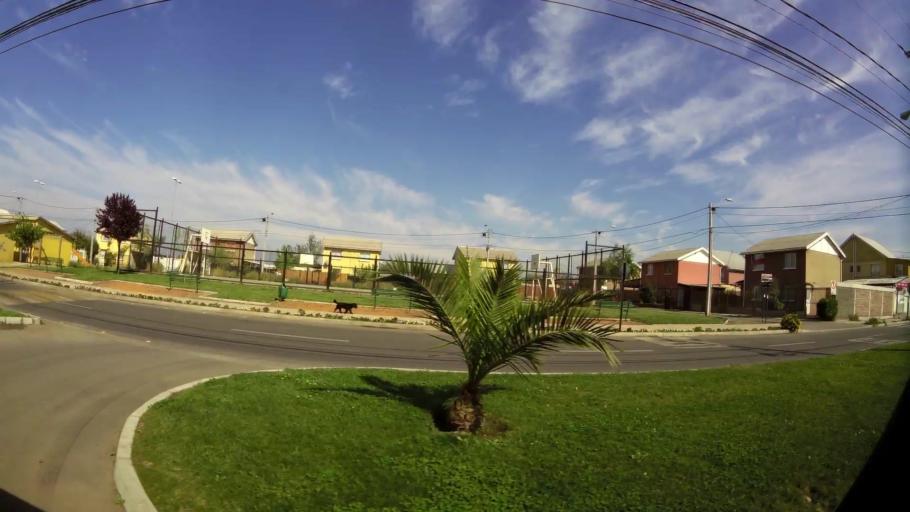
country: CL
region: Santiago Metropolitan
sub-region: Provincia de Talagante
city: El Monte
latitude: -33.6814
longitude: -70.9545
